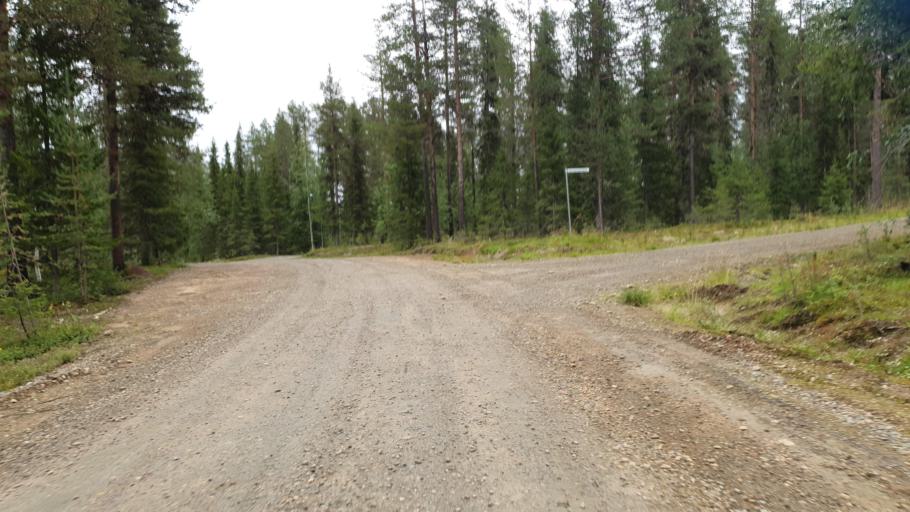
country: FI
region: Lapland
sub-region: Tunturi-Lappi
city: Kolari
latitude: 67.6002
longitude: 24.1959
